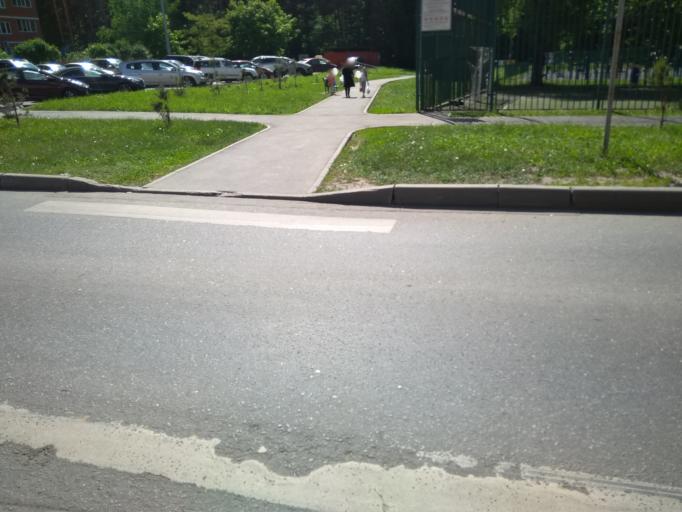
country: RU
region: Moskovskaya
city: Troitsk
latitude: 55.4858
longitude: 37.3038
